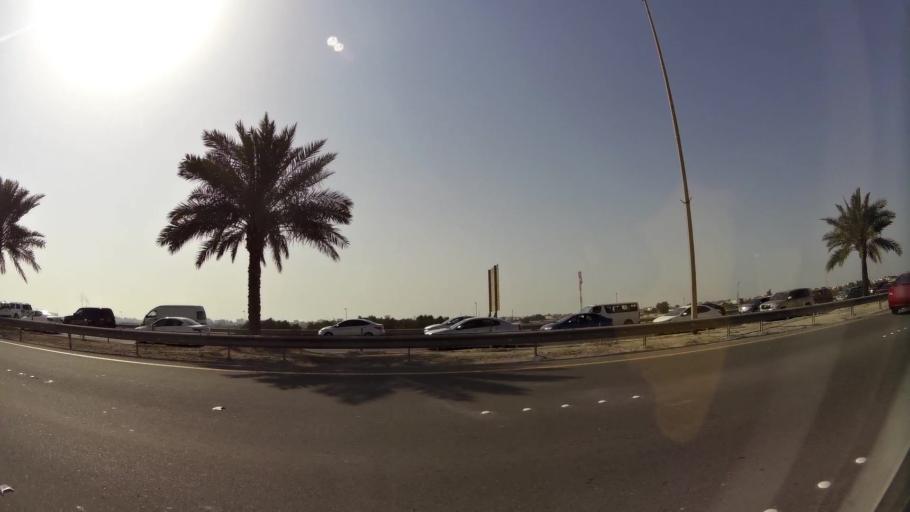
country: BH
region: Northern
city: Madinat `Isa
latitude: 26.1891
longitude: 50.5043
